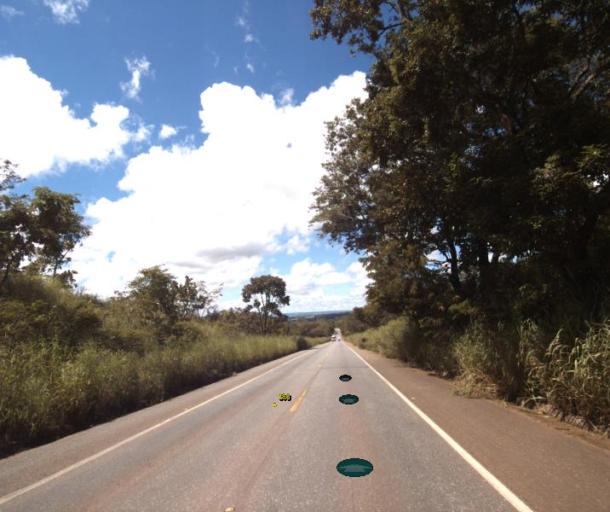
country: BR
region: Goias
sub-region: Petrolina De Goias
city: Petrolina de Goias
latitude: -15.9527
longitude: -49.1859
